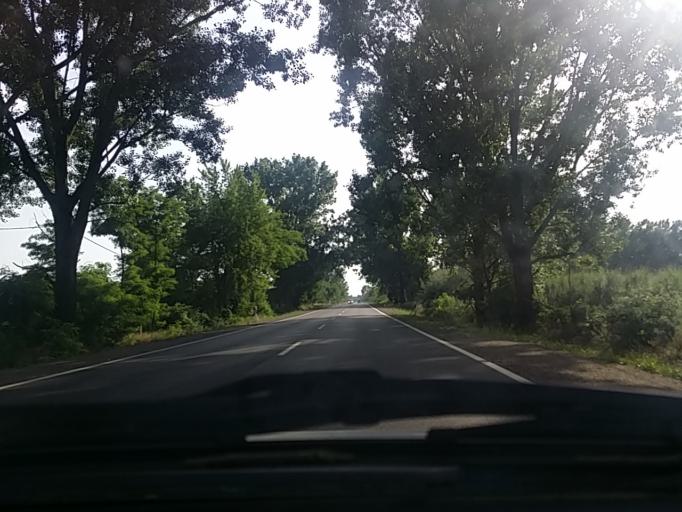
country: HU
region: Jasz-Nagykun-Szolnok
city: Jaszbereny
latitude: 47.4554
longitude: 19.8348
